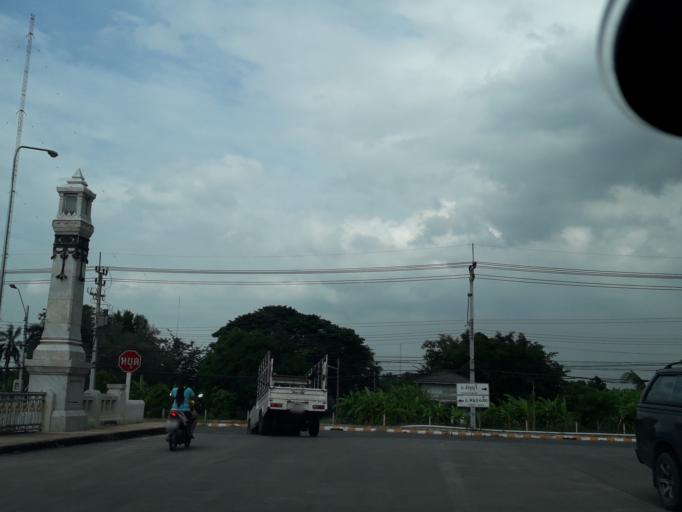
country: TH
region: Pathum Thani
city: Thanyaburi
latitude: 14.0713
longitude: 100.7098
